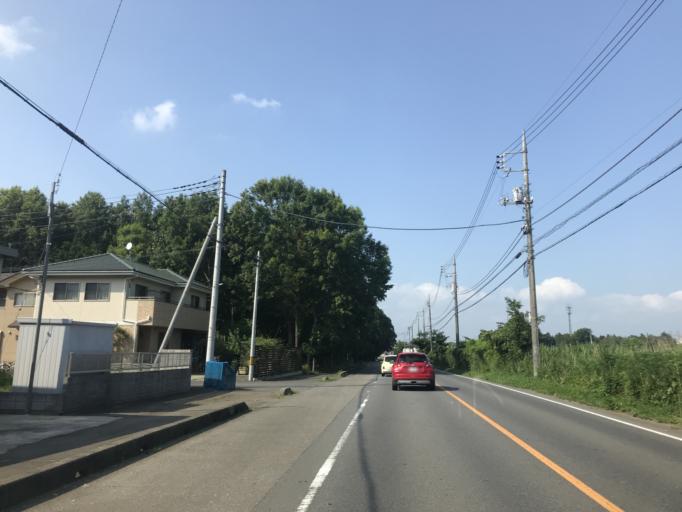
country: JP
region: Ibaraki
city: Naka
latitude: 36.0635
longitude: 140.0934
